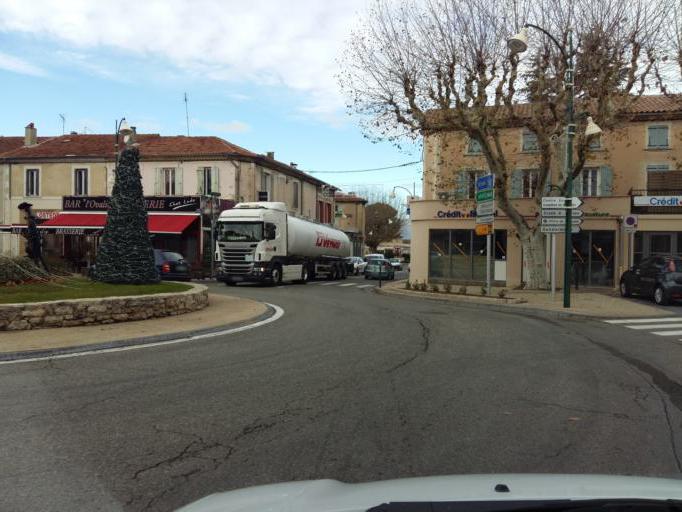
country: FR
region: Provence-Alpes-Cote d'Azur
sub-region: Departement du Vaucluse
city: Valreas
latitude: 44.3865
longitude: 4.9909
